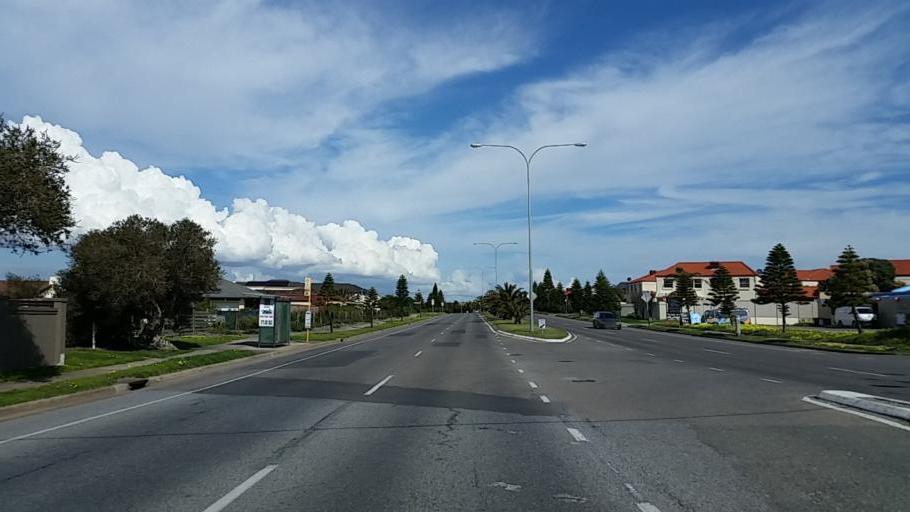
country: AU
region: South Australia
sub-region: Charles Sturt
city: West Lakes Shore
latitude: -34.8645
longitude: 138.4797
